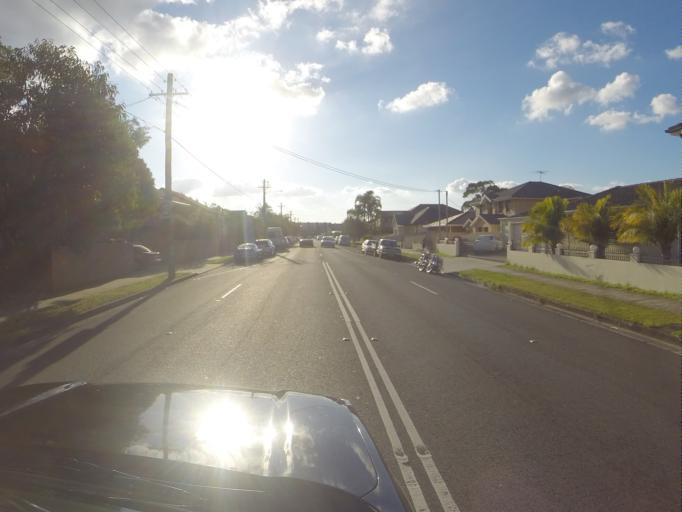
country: AU
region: New South Wales
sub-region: Kogarah
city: Kogarah Bay
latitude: -33.9669
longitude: 151.1131
